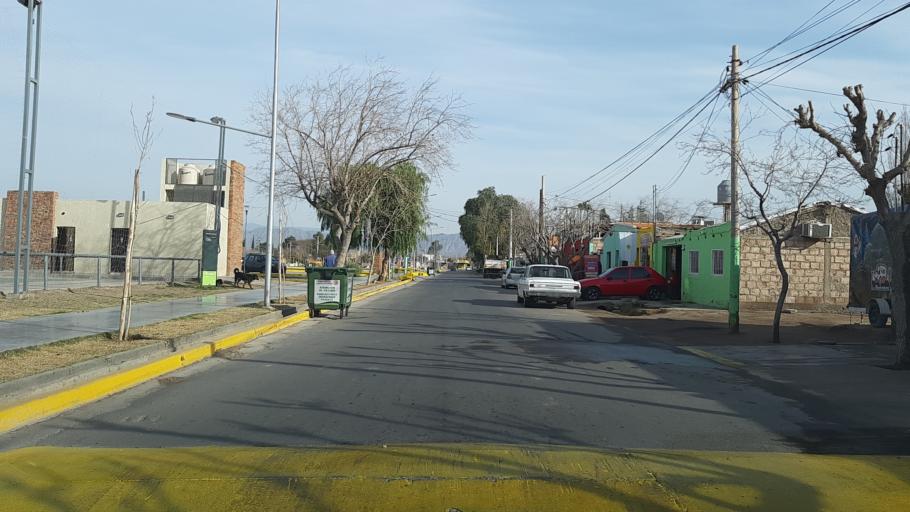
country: AR
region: San Juan
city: San Juan
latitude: -31.5322
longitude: -68.5910
